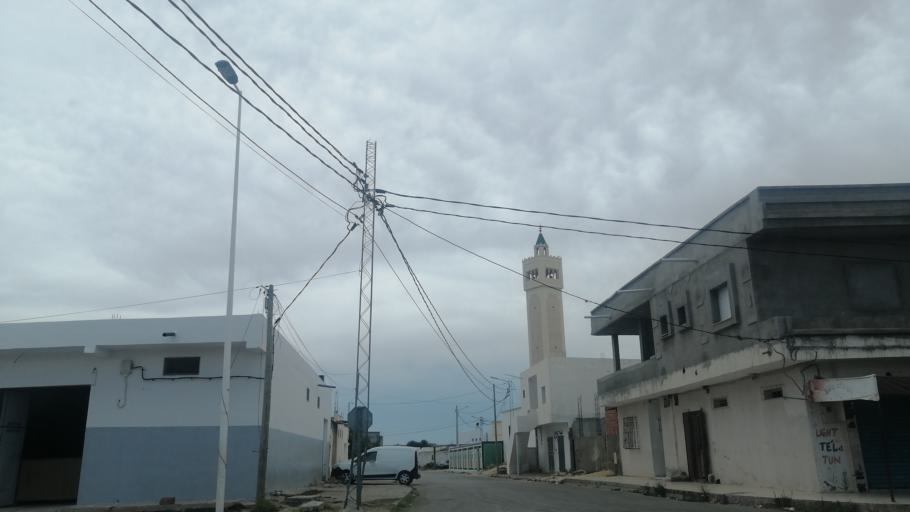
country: TN
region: Al Qayrawan
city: Sbikha
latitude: 36.1260
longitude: 10.0926
